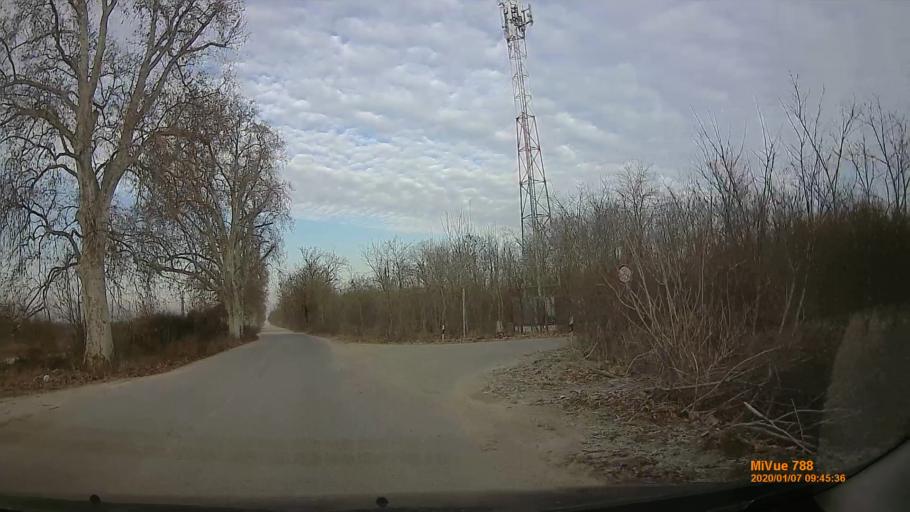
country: HU
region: Gyor-Moson-Sopron
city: Rajka
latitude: 47.9417
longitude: 17.1641
